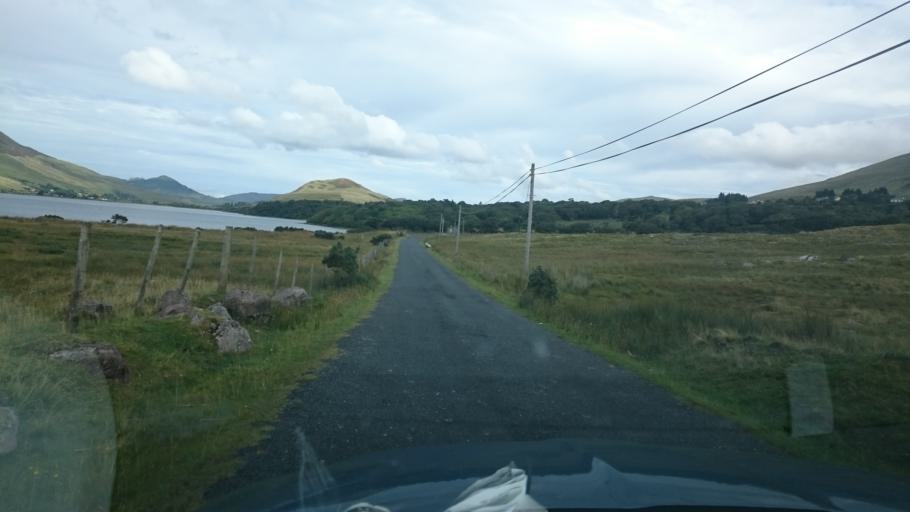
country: IE
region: Connaught
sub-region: Maigh Eo
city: Westport
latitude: 53.9420
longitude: -9.5681
